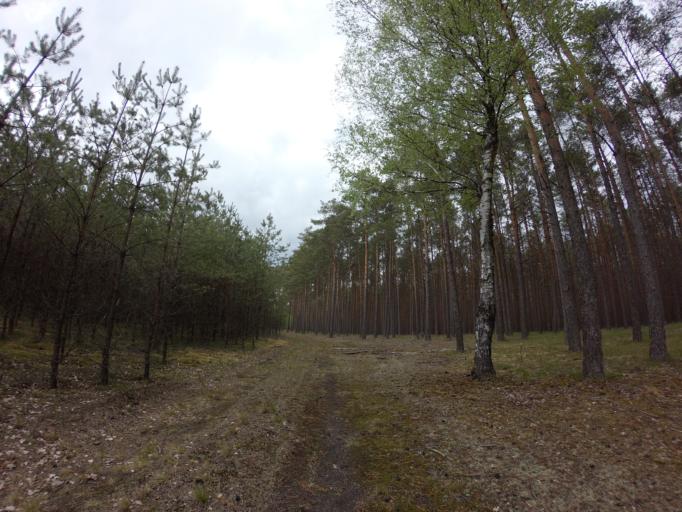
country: PL
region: West Pomeranian Voivodeship
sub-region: Powiat drawski
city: Kalisz Pomorski
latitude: 53.1902
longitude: 15.9819
